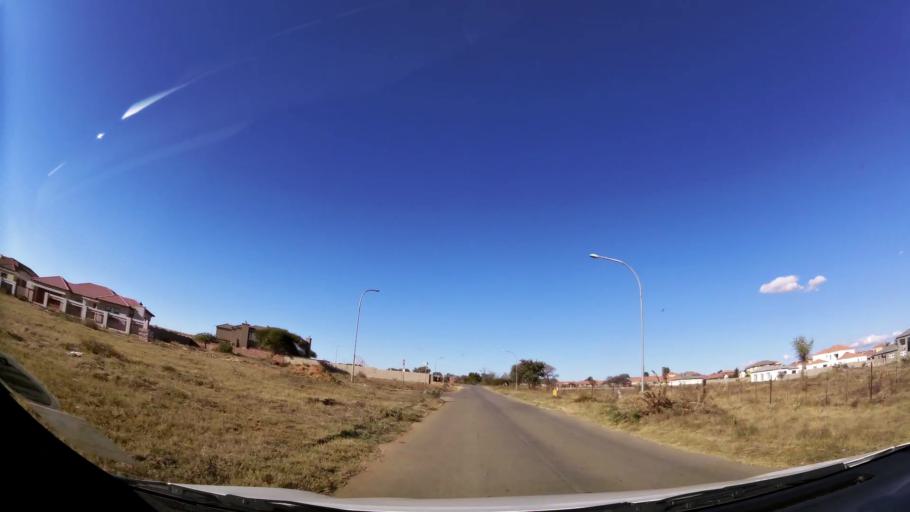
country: ZA
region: Limpopo
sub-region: Capricorn District Municipality
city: Polokwane
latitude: -23.9036
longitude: 29.5051
